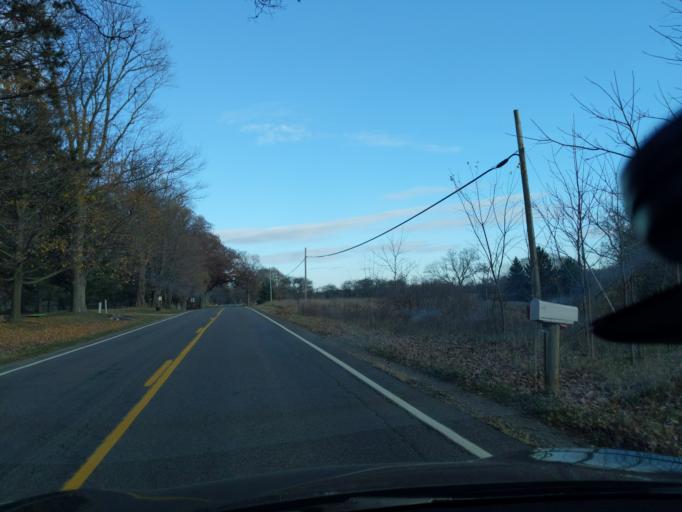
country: US
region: Michigan
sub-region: Ingham County
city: Williamston
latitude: 42.7153
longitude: -84.3424
